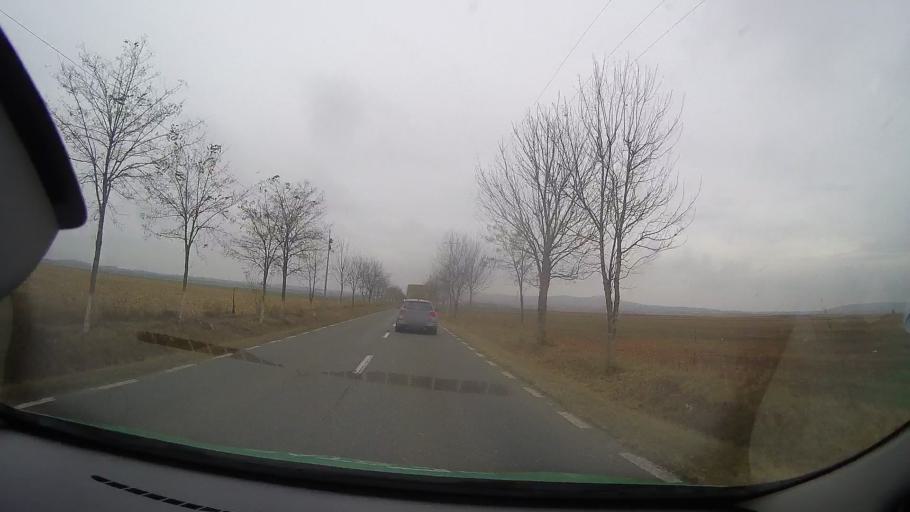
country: RO
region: Prahova
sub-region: Oras Baicoi
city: Liliesti
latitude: 45.0051
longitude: 25.8836
